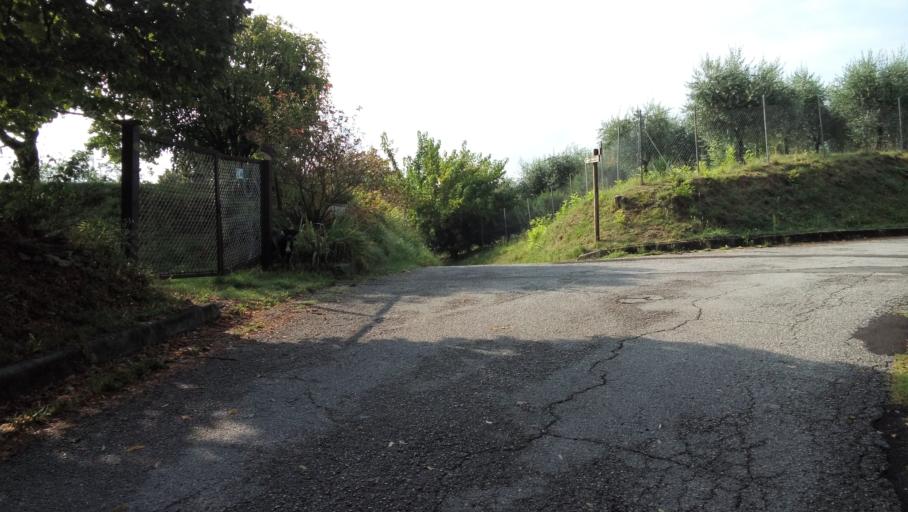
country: IT
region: Veneto
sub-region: Provincia di Vicenza
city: Monteviale
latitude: 45.5461
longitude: 11.4586
